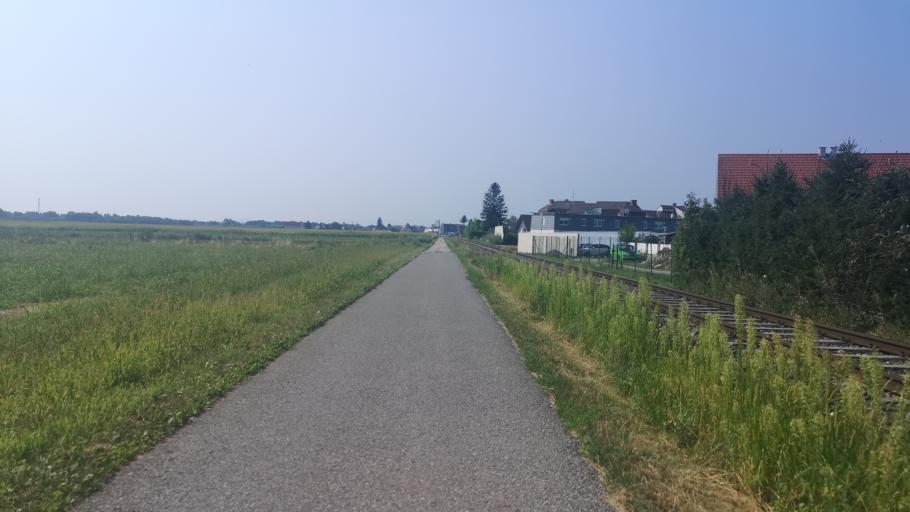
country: AT
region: Styria
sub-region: Politischer Bezirk Graz-Umgebung
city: Seiersberg
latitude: 47.0064
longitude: 15.4018
